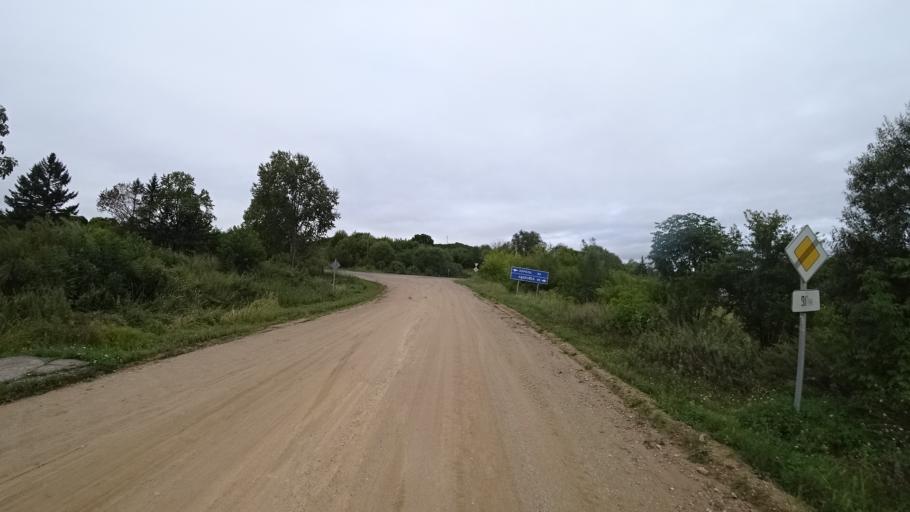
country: RU
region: Primorskiy
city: Rettikhovka
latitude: 44.1672
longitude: 132.7377
